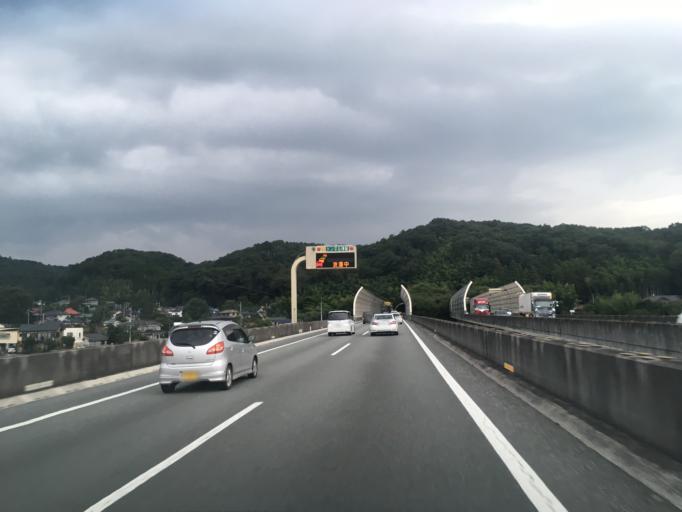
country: JP
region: Tokyo
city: Fussa
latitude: 35.7408
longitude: 139.2817
